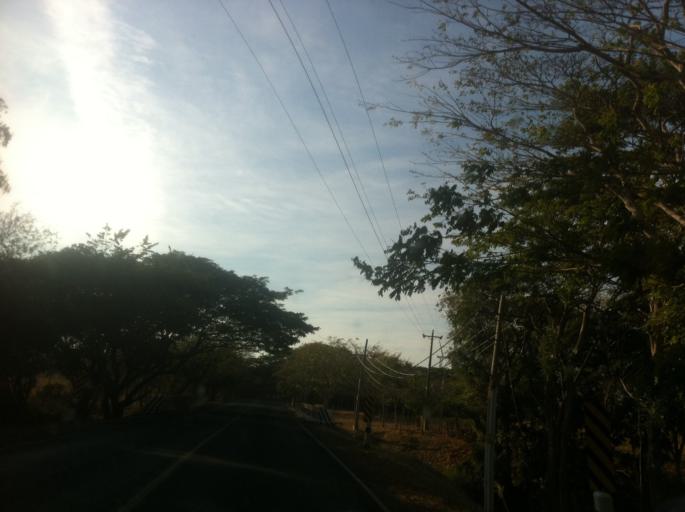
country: NI
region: Rivas
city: Rivas
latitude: 11.3170
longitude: -85.7107
